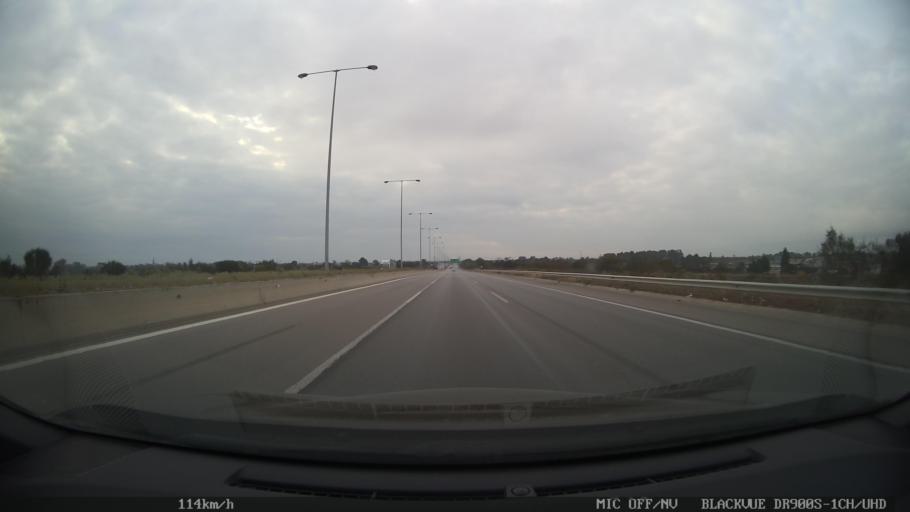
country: GR
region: Central Macedonia
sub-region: Nomos Thessalonikis
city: Nea Magnisia
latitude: 40.6656
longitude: 22.8363
